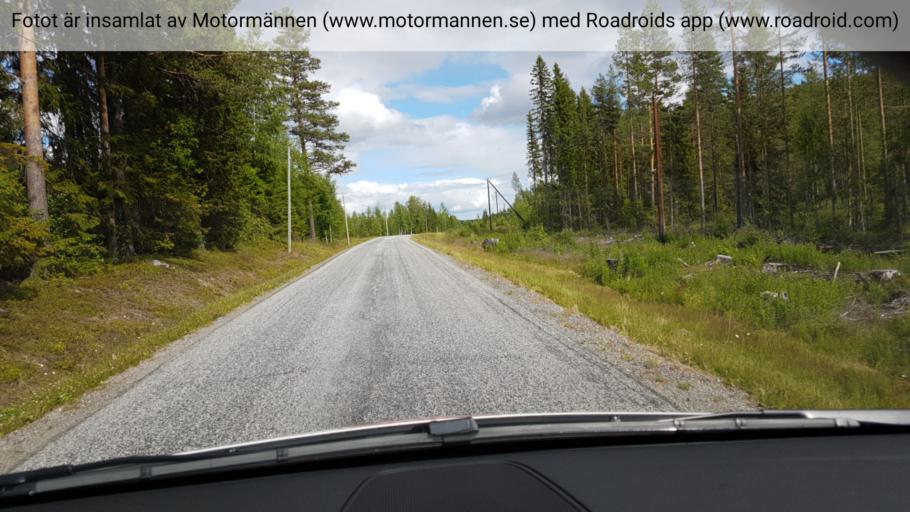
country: SE
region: Vaesterbotten
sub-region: Dorotea Kommun
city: Dorotea
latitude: 64.1263
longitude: 16.2782
